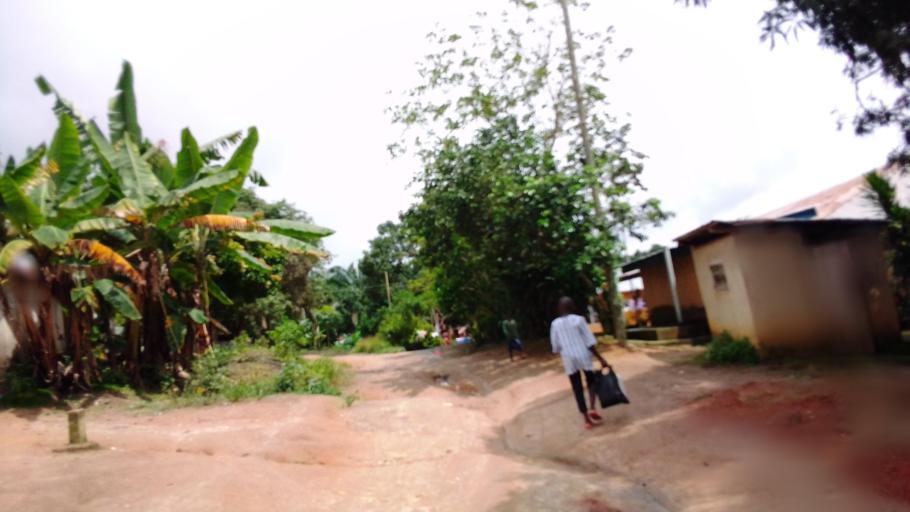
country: SL
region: Eastern Province
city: Kenema
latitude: 7.8655
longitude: -11.1768
